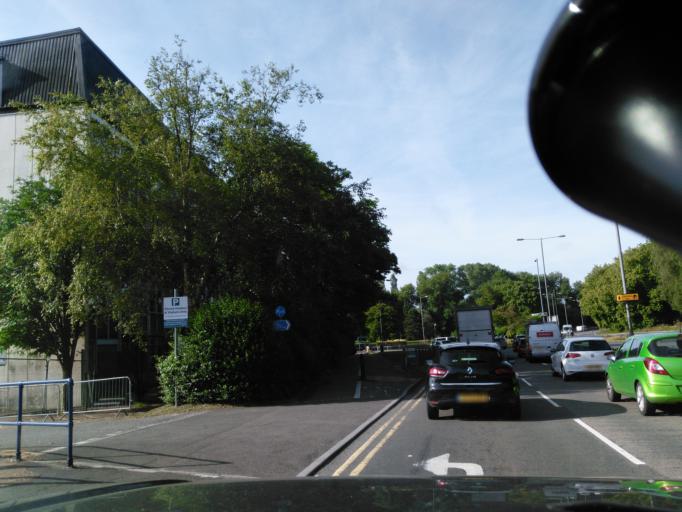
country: GB
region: England
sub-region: Wiltshire
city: Salisbury
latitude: 51.0652
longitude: -1.7889
